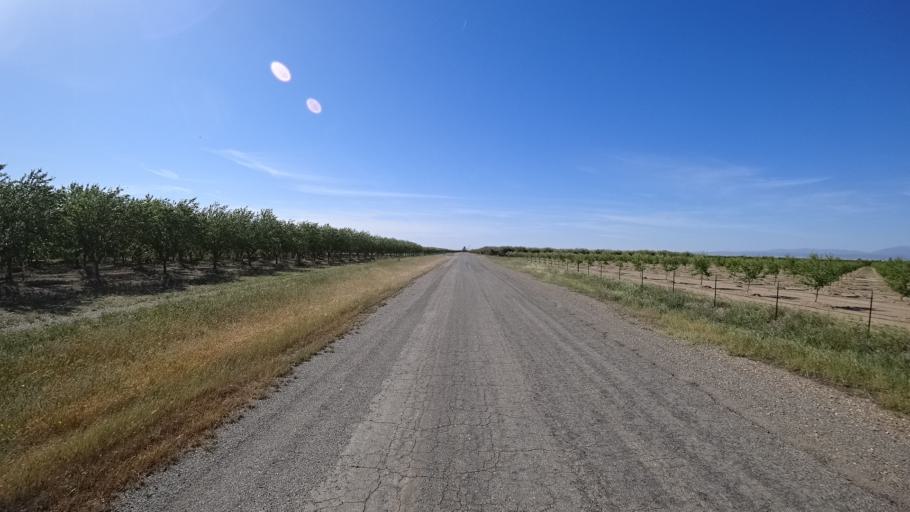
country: US
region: California
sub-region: Glenn County
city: Willows
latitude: 39.6325
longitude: -122.1600
